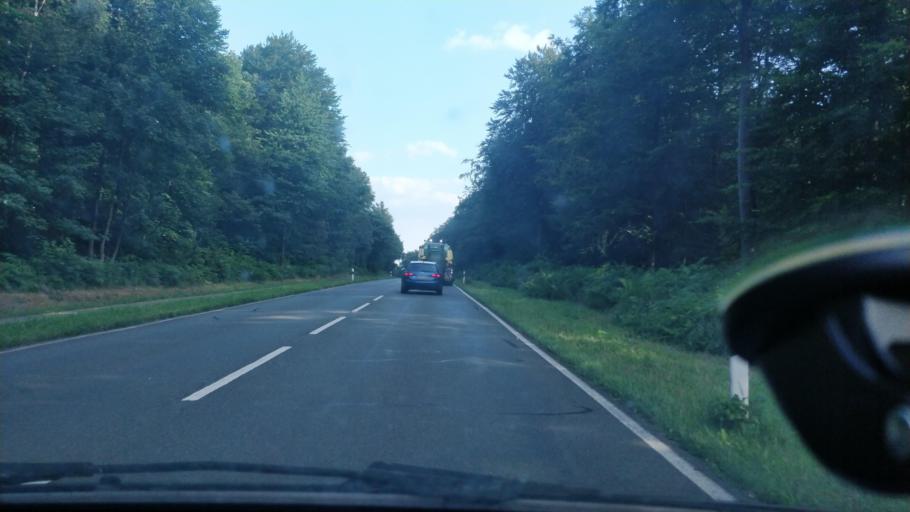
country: DE
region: North Rhine-Westphalia
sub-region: Regierungsbezirk Dusseldorf
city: Alpen
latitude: 51.5415
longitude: 6.5061
